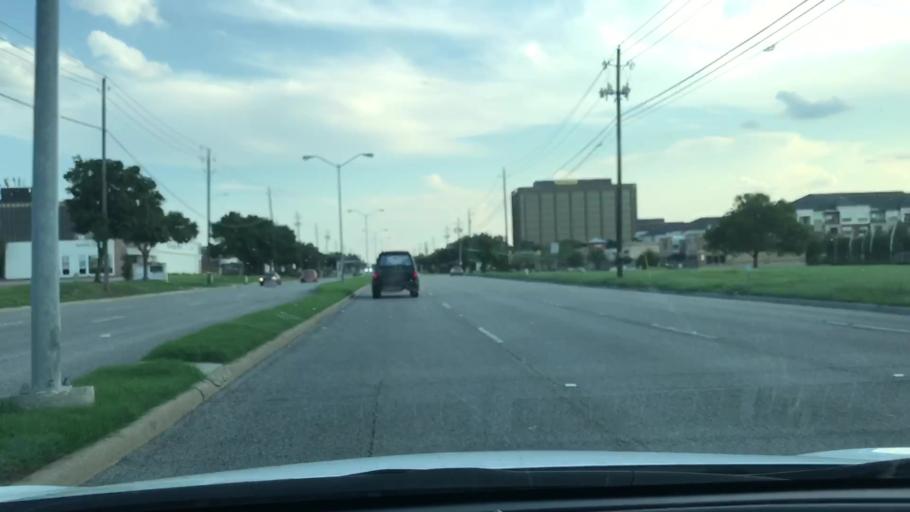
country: US
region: Texas
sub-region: Dallas County
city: Addison
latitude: 32.9364
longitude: -96.8390
